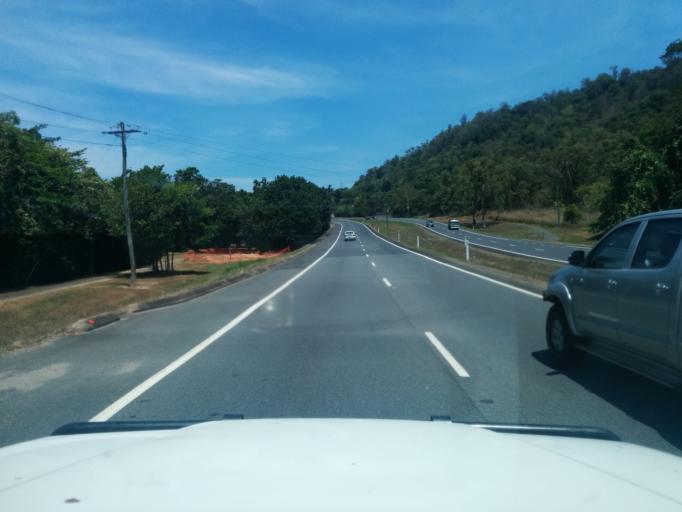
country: AU
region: Queensland
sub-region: Cairns
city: Redlynch
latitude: -16.9065
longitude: 145.7113
